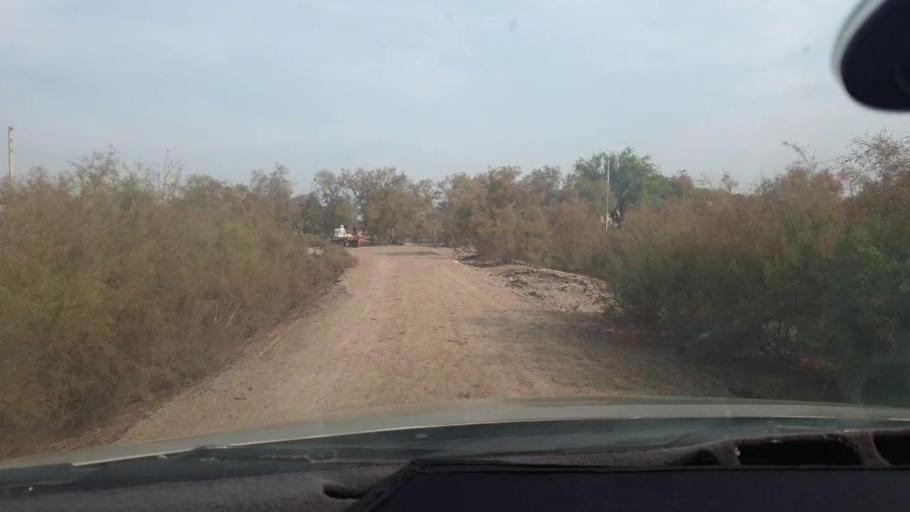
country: PK
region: Balochistan
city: Jhatpat
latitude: 28.3708
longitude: 68.4036
